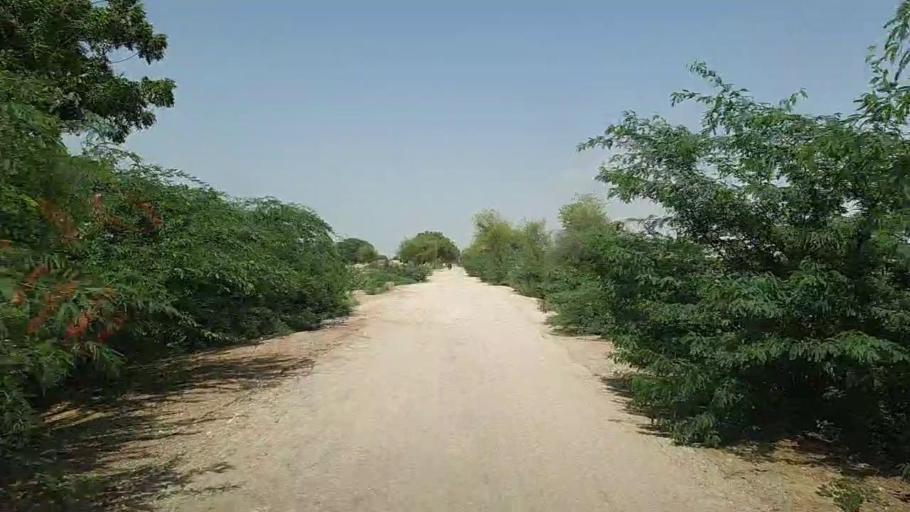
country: PK
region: Sindh
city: Pad Idan
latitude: 26.7905
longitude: 68.3524
